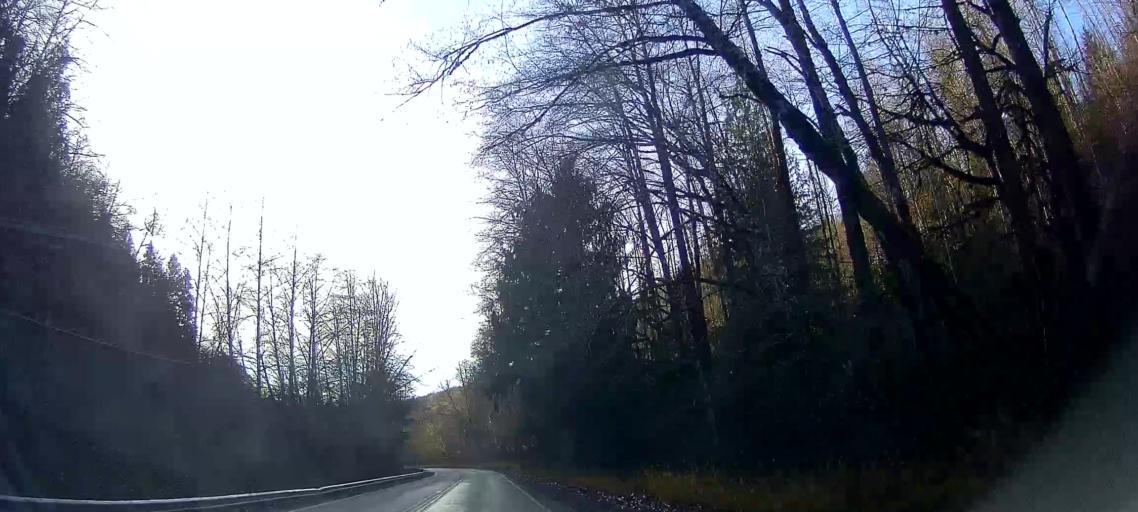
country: US
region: Washington
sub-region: Skagit County
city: Sedro-Woolley
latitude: 48.5481
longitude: -121.8737
